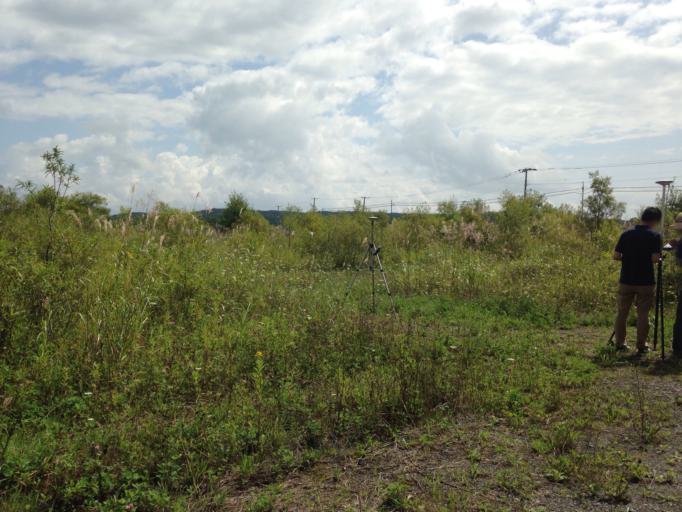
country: JP
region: Hokkaido
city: Tobetsu
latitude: 43.2575
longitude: 141.5292
